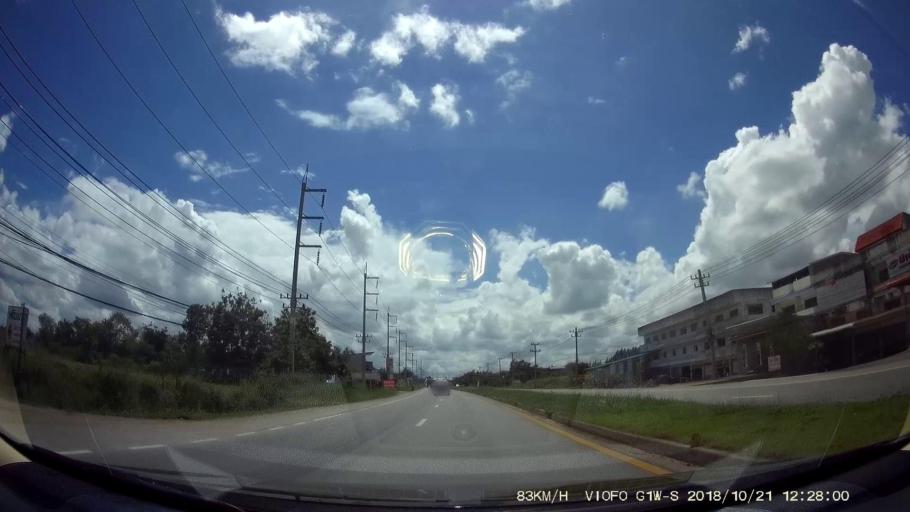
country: TH
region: Nakhon Ratchasima
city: Dan Khun Thot
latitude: 15.1948
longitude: 101.7620
